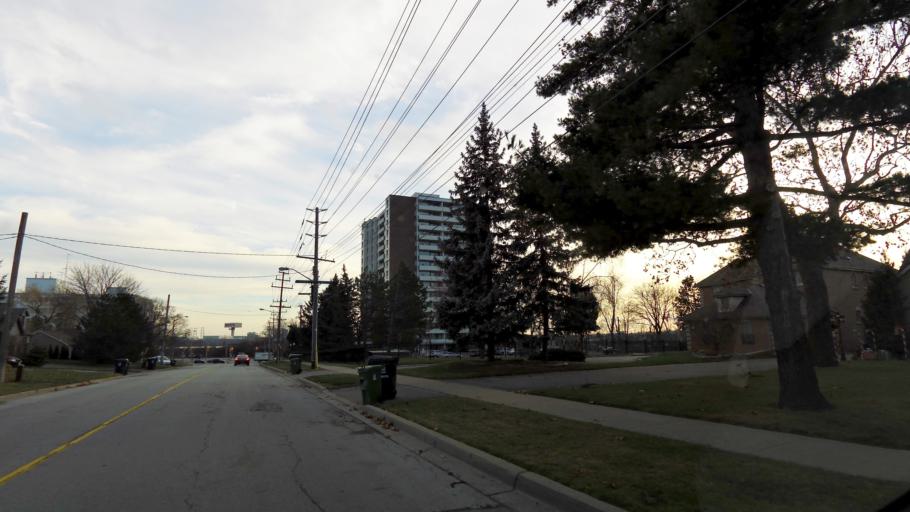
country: CA
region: Ontario
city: Etobicoke
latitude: 43.6293
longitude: -79.5632
